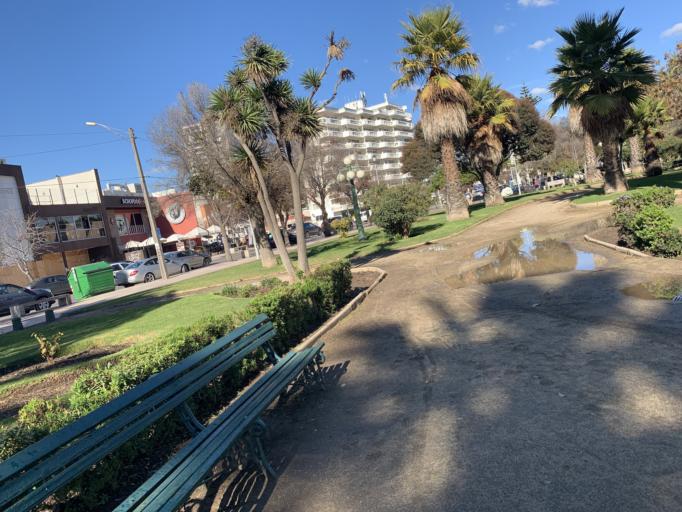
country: CL
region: Valparaiso
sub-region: Provincia de Valparaiso
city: Vina del Mar
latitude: -33.0176
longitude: -71.5587
